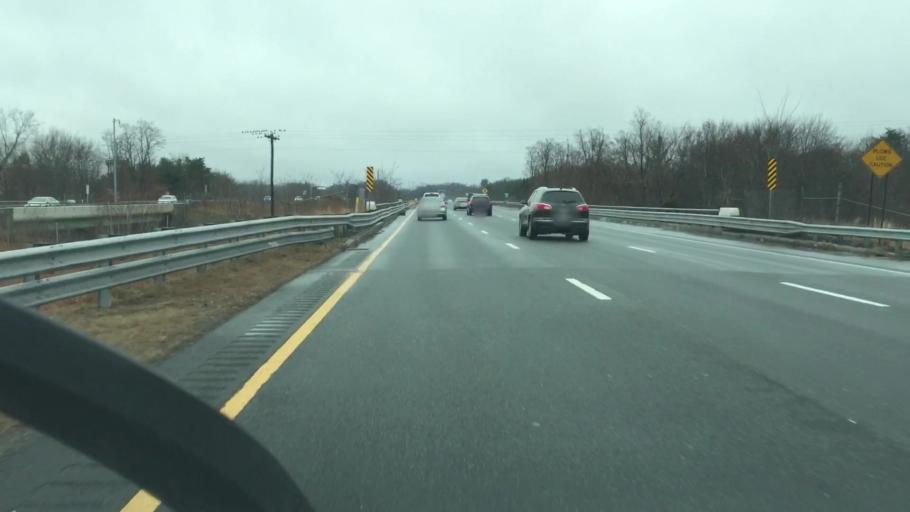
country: US
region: Massachusetts
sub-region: Worcester County
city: Milford
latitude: 42.1470
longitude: -71.4841
